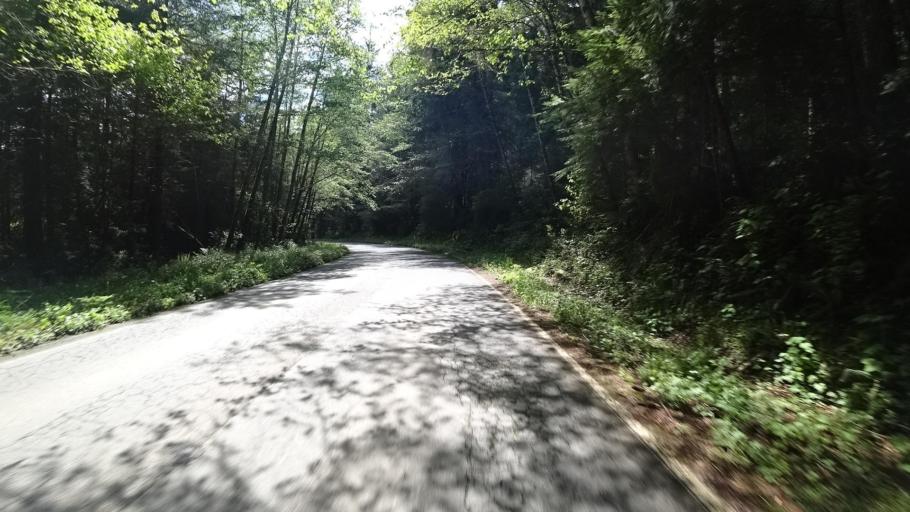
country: US
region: California
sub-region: Humboldt County
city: McKinleyville
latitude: 40.9699
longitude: -124.0597
